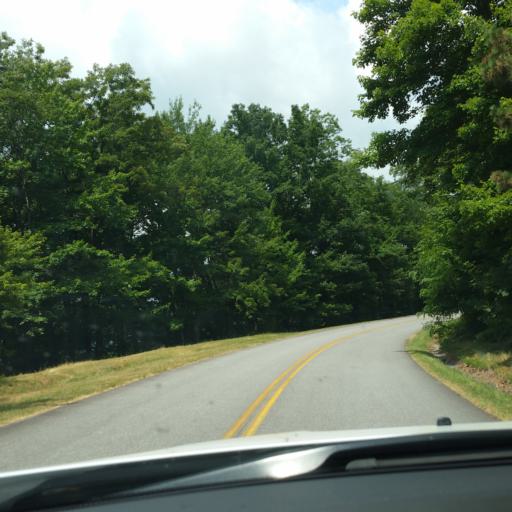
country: US
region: North Carolina
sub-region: Buncombe County
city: Avery Creek
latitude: 35.4480
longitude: -82.6474
